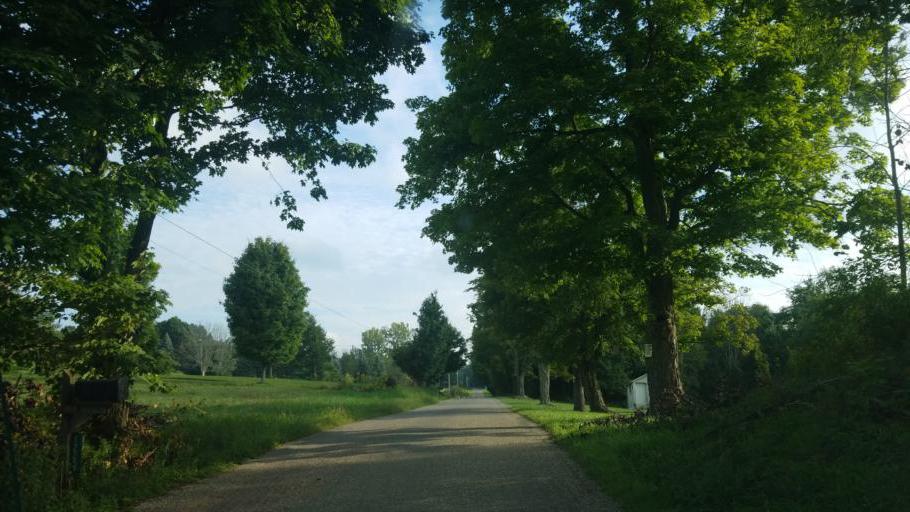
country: US
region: Ohio
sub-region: Medina County
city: Lodi
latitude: 40.9484
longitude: -82.0041
